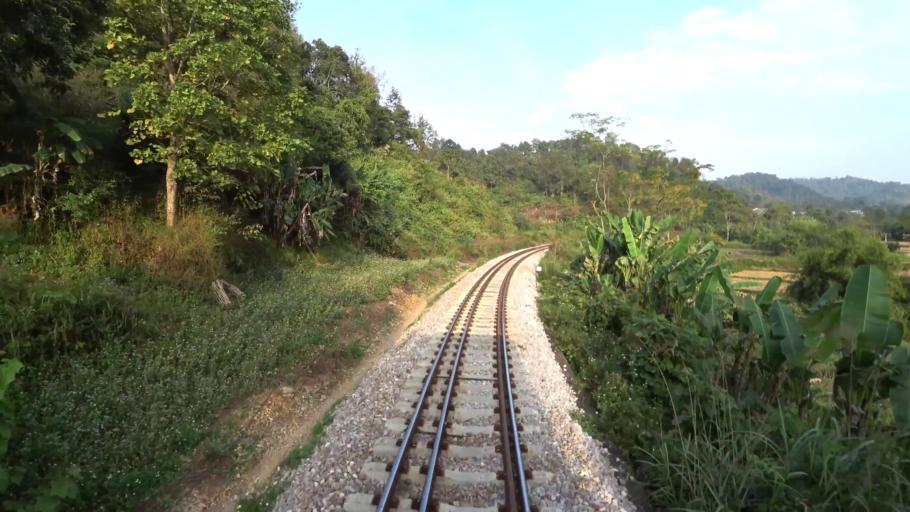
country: VN
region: Lang Son
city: Thi Tran Cao Loc
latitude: 21.9236
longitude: 106.7153
